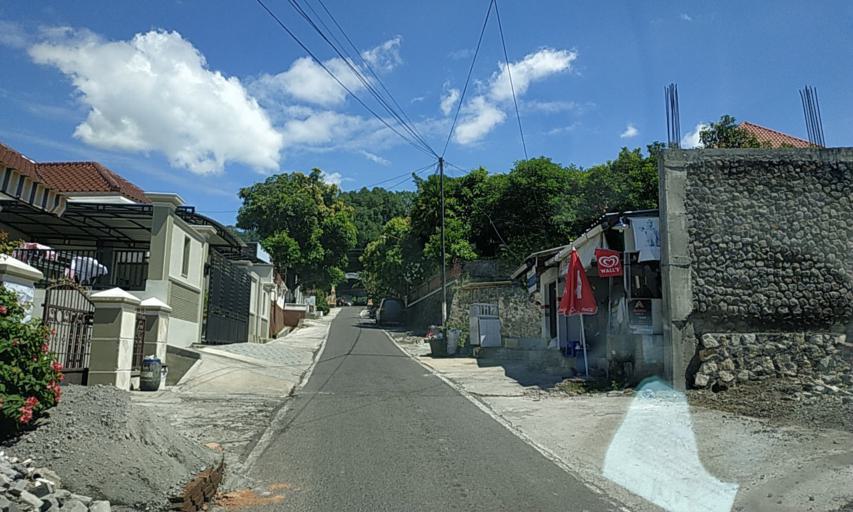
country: ID
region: Central Java
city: Selogiri
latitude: -7.8126
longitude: 110.9252
